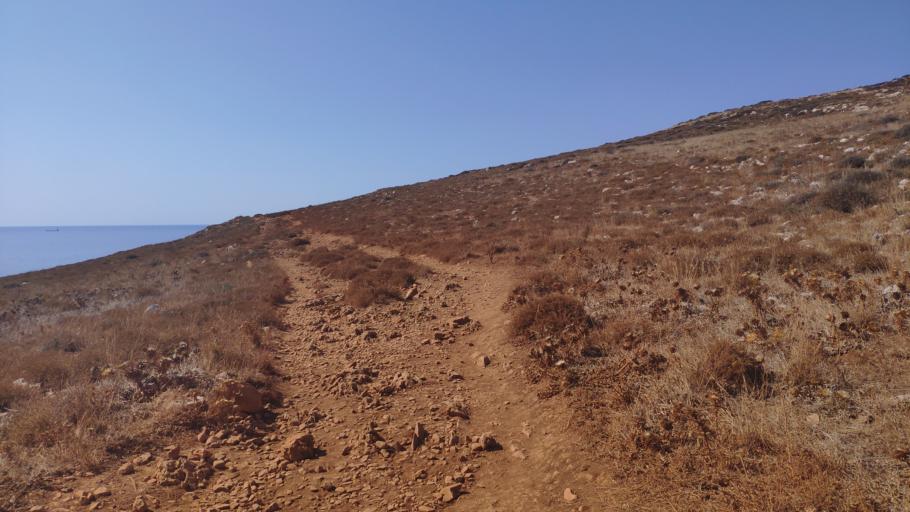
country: GR
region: Peloponnese
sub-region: Nomos Lakonias
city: Gytheio
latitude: 36.3930
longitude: 22.4836
